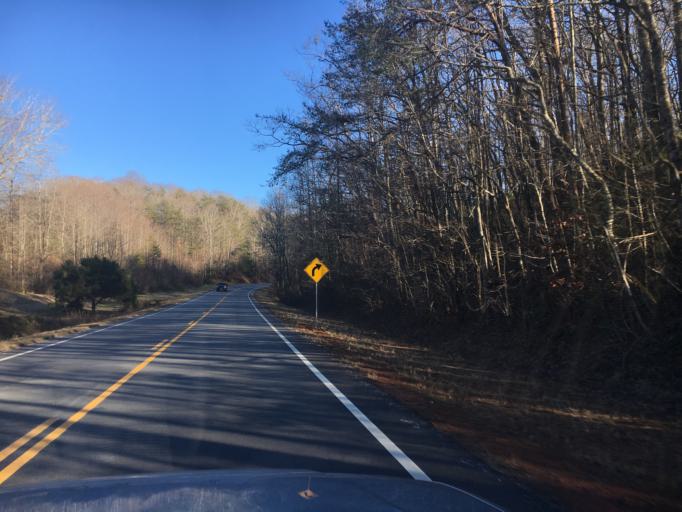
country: US
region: Georgia
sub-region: White County
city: Cleveland
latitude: 34.6684
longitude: -83.8620
